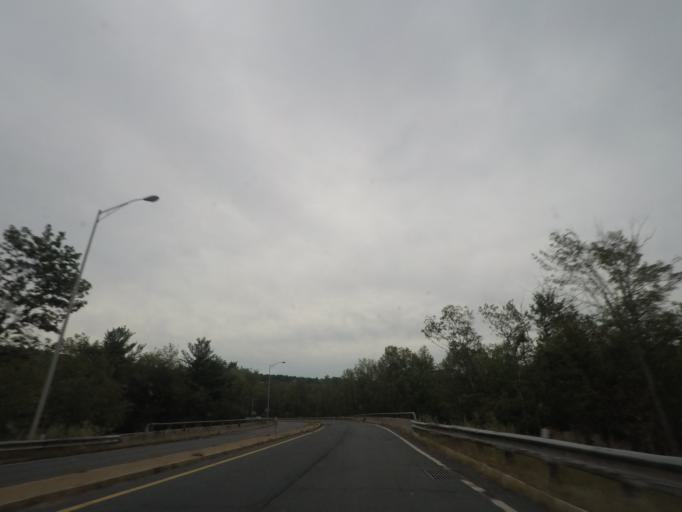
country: US
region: Massachusetts
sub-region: Hampden County
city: Palmer
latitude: 42.1705
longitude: -72.3307
